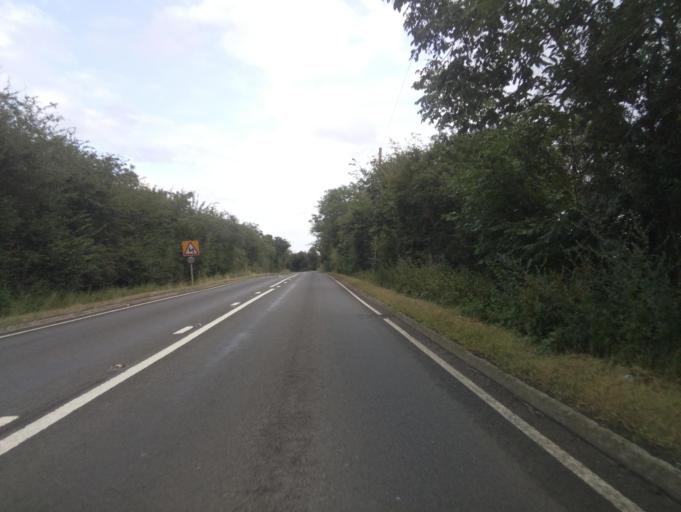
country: GB
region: England
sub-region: Warwickshire
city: Southam
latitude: 52.2629
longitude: -1.3856
